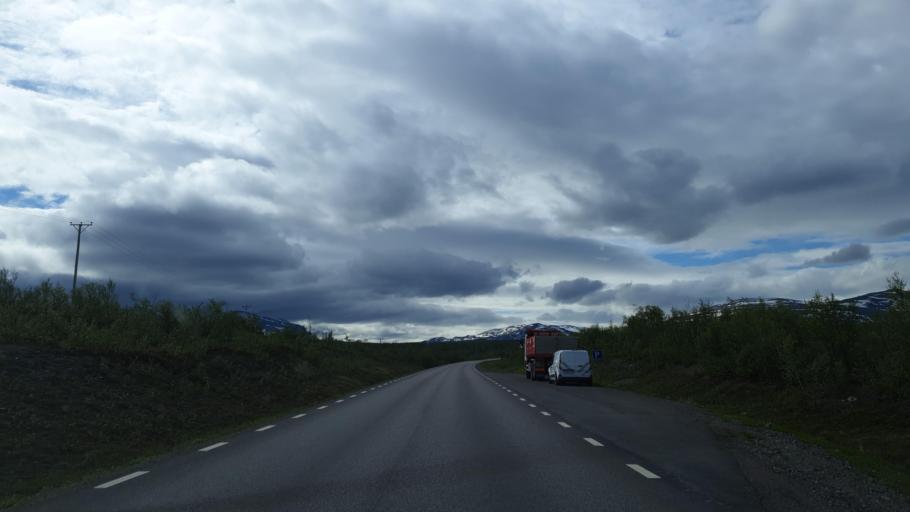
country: NO
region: Troms
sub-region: Bardu
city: Setermoen
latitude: 68.3476
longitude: 18.9643
